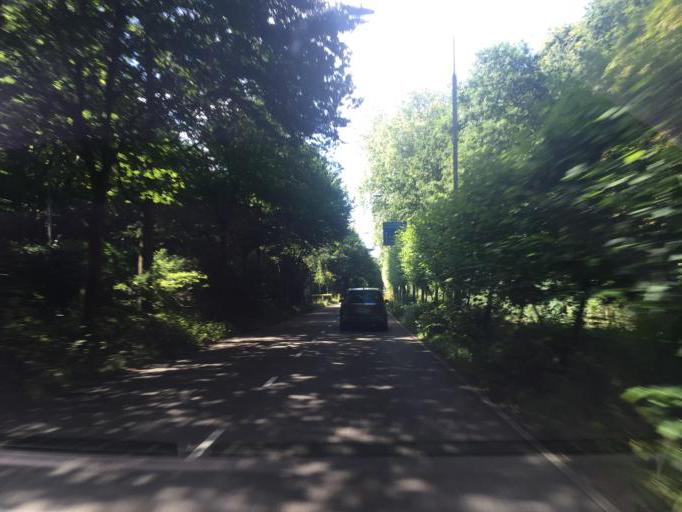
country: NL
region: North Holland
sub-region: Gemeente Haarlem
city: Haarlem
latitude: 52.3674
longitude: 4.6282
